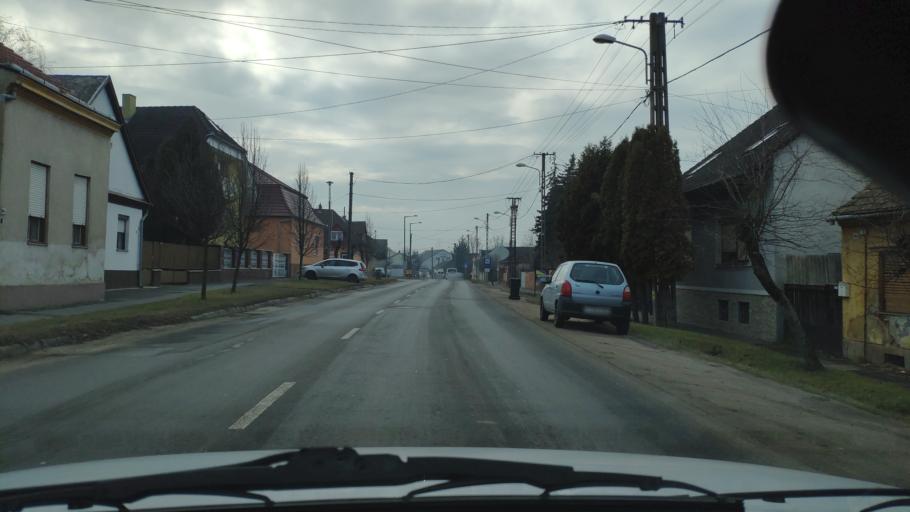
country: HU
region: Zala
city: Nagykanizsa
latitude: 46.4642
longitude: 16.9861
